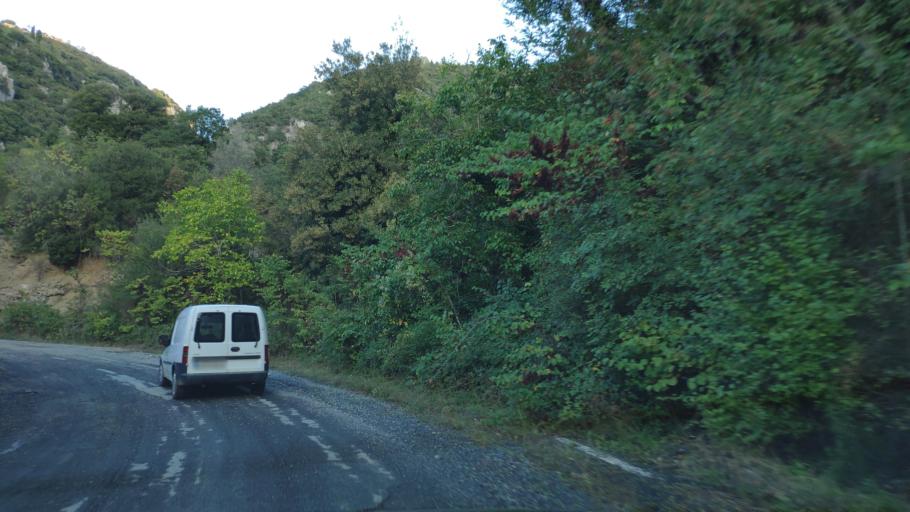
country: GR
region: Peloponnese
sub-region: Nomos Arkadias
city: Dimitsana
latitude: 37.5748
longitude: 22.0521
